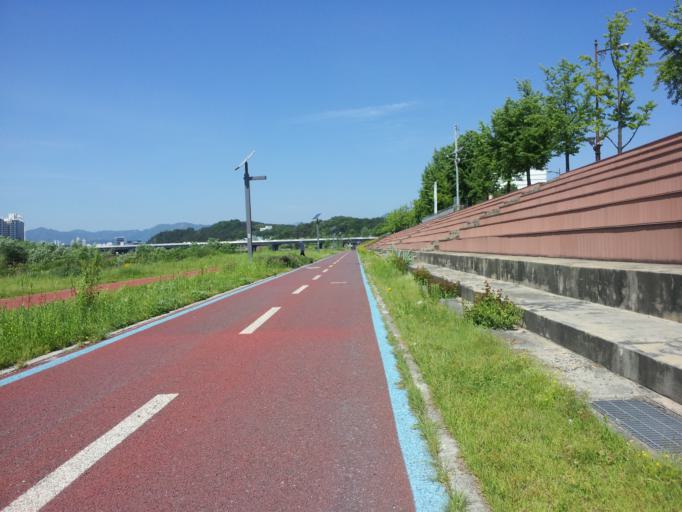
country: KR
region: Daejeon
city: Songgang-dong
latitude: 36.3741
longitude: 127.3854
